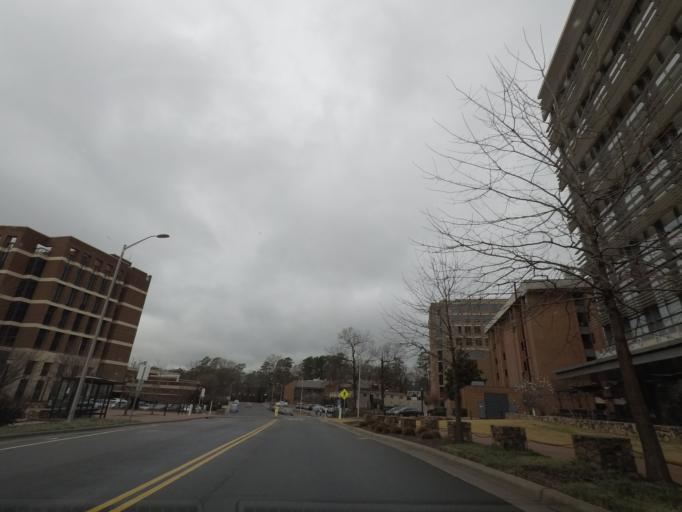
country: US
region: North Carolina
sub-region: Orange County
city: Chapel Hill
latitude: 35.9022
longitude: -79.0540
